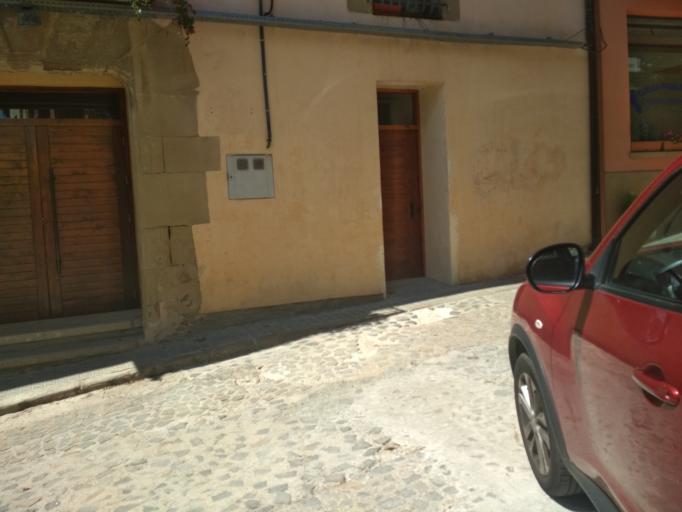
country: ES
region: Catalonia
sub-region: Provincia de Barcelona
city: Castelltercol
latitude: 41.7512
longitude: 2.1207
